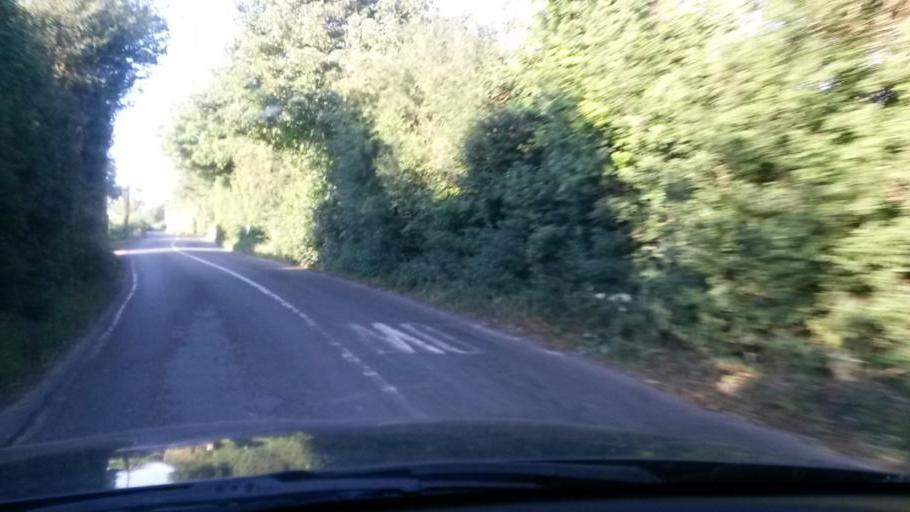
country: IE
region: Leinster
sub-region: Fingal County
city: Blanchardstown
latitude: 53.4339
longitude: -6.3602
